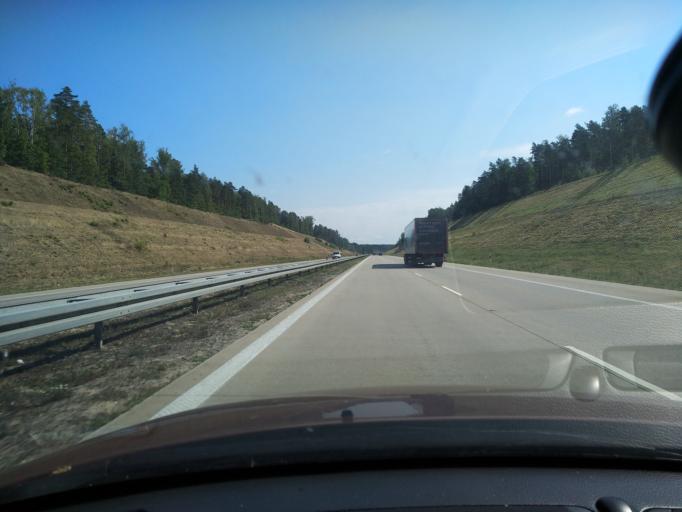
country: PL
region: Lower Silesian Voivodeship
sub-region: Powiat lubanski
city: Pisarzowice
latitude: 51.2128
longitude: 15.1972
